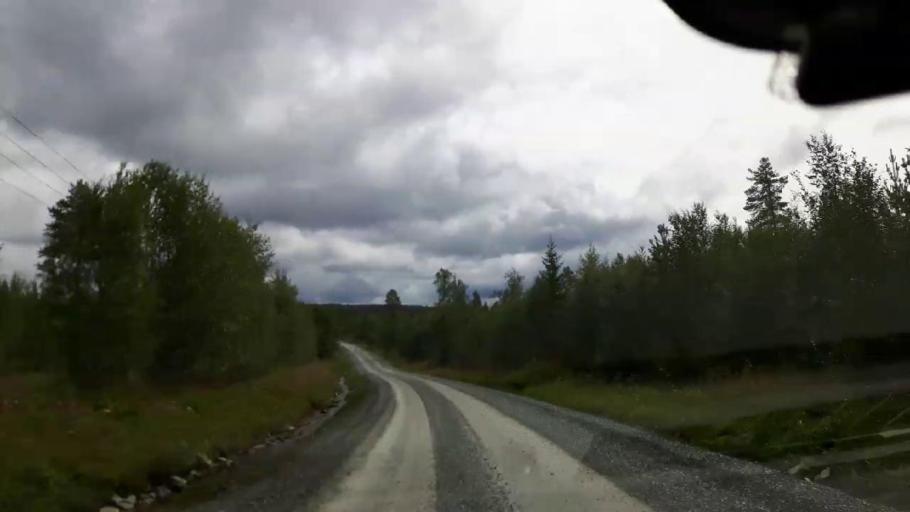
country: SE
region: Jaemtland
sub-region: Krokoms Kommun
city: Valla
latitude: 63.6060
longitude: 14.1244
